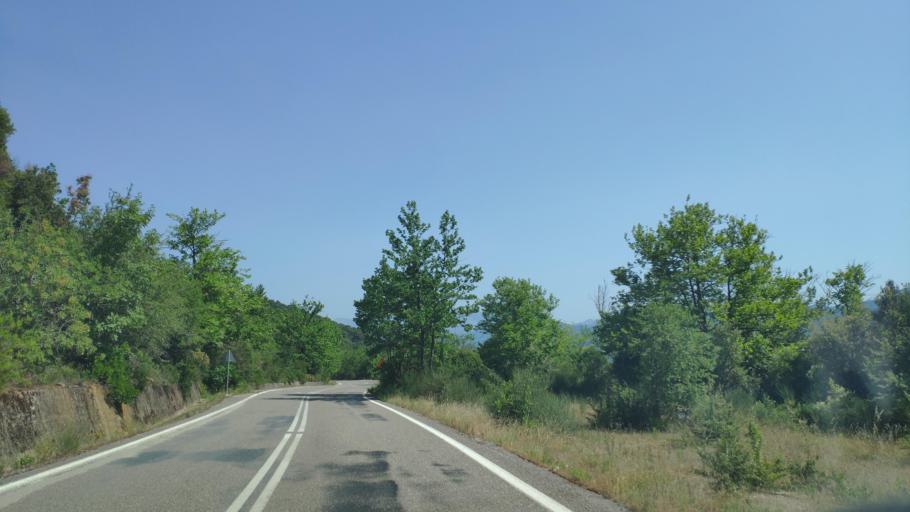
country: GR
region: West Greece
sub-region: Nomos Aitolias kai Akarnanias
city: Lepenou
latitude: 38.8028
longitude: 21.3332
